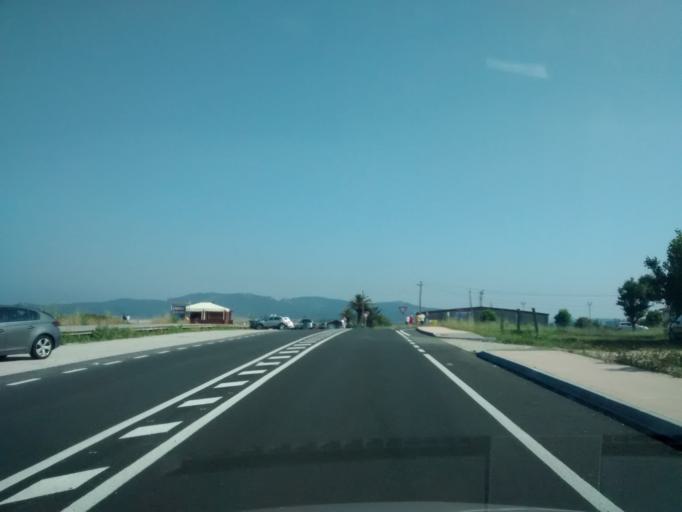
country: ES
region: Galicia
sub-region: Provincia de Pontevedra
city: O Grove
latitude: 42.4363
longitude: -8.8704
